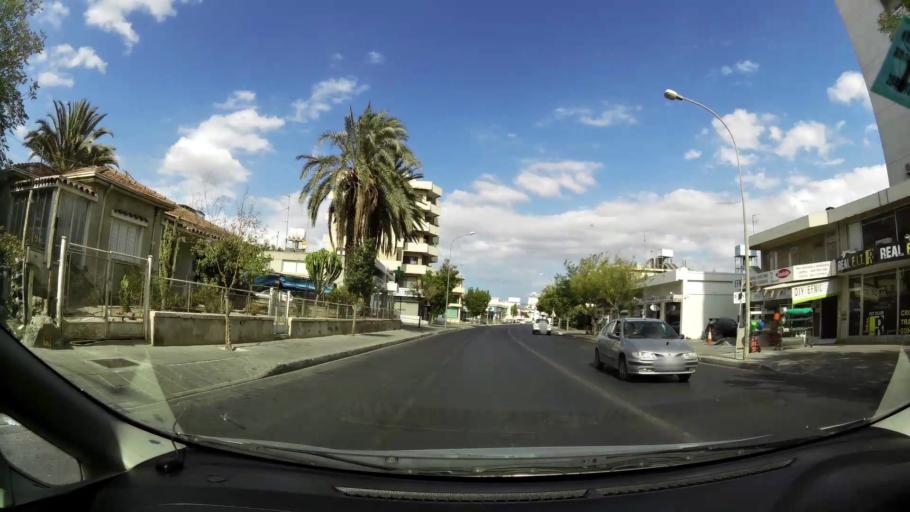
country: CY
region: Lefkosia
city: Nicosia
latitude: 35.1824
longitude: 33.3864
